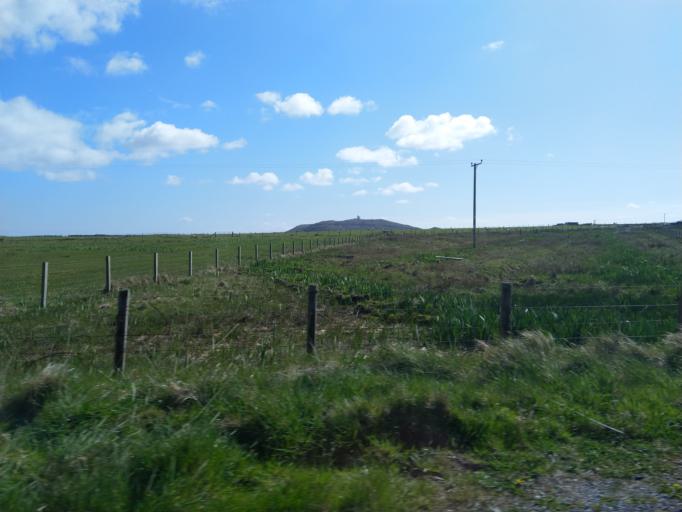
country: GB
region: Scotland
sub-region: Eilean Siar
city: Barra
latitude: 56.4837
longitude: -6.9160
